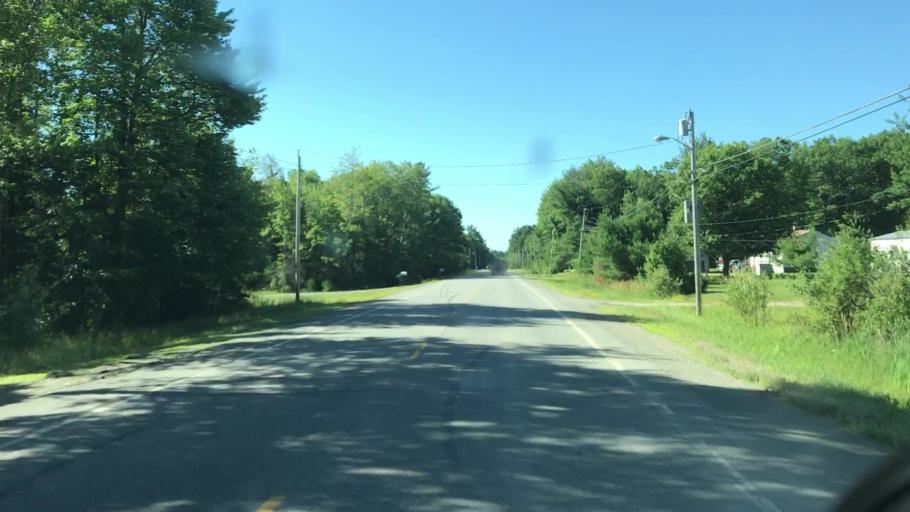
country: US
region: Maine
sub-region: Penobscot County
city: Howland
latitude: 45.2650
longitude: -68.6385
